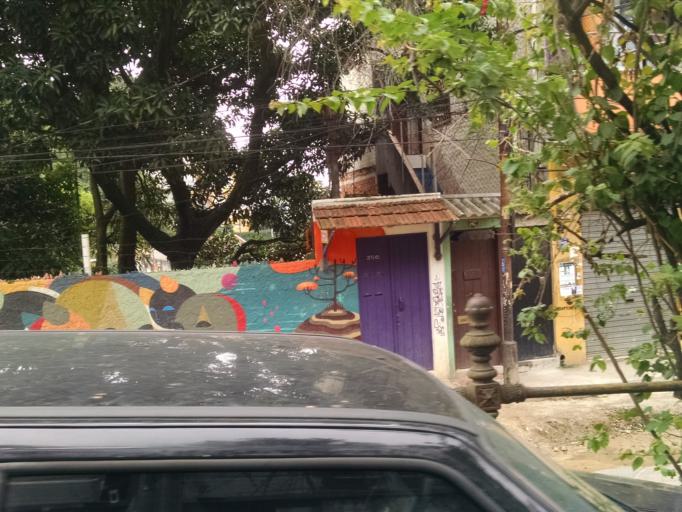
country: BR
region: Rio de Janeiro
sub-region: Rio De Janeiro
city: Rio de Janeiro
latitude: -22.9213
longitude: -43.1850
